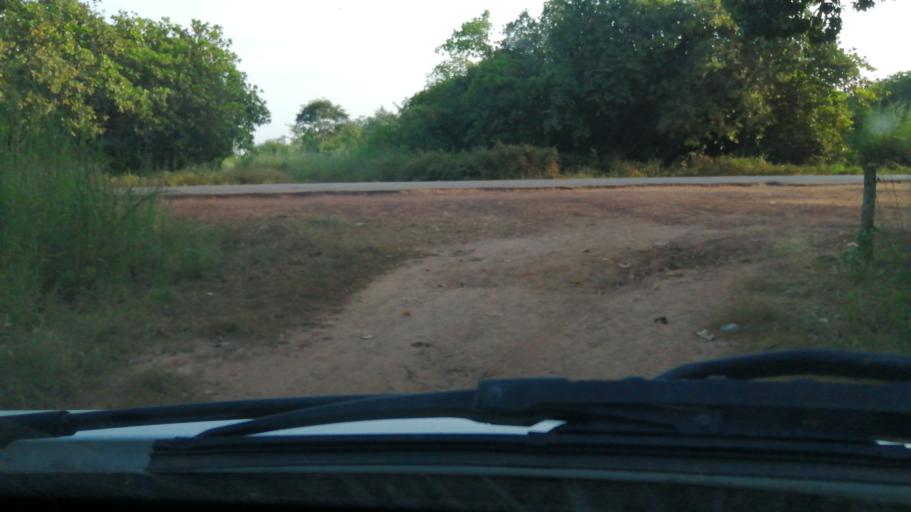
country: GW
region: Bissau
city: Bissau
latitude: 11.9794
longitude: -15.4679
